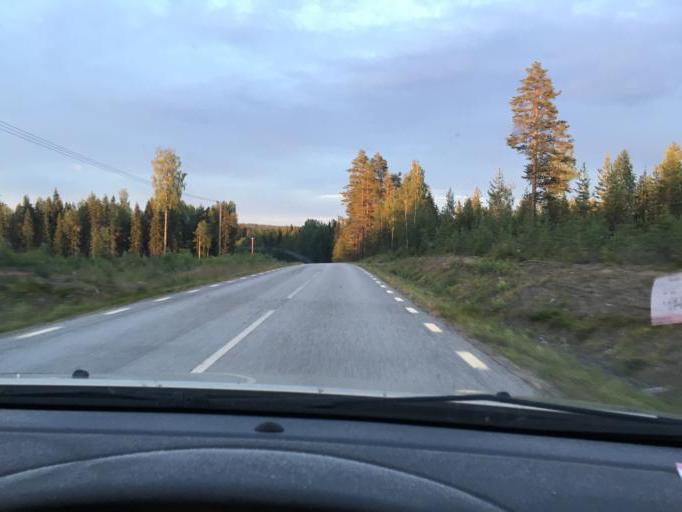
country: SE
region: Norrbotten
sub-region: Kalix Kommun
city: Toere
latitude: 66.0529
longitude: 22.5404
